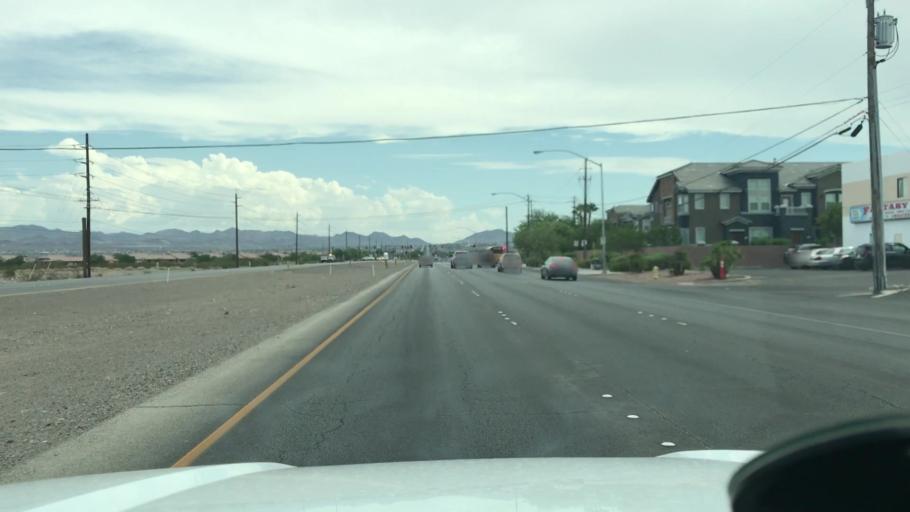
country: US
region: Nevada
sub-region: Clark County
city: Henderson
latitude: 36.0784
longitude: -115.0258
